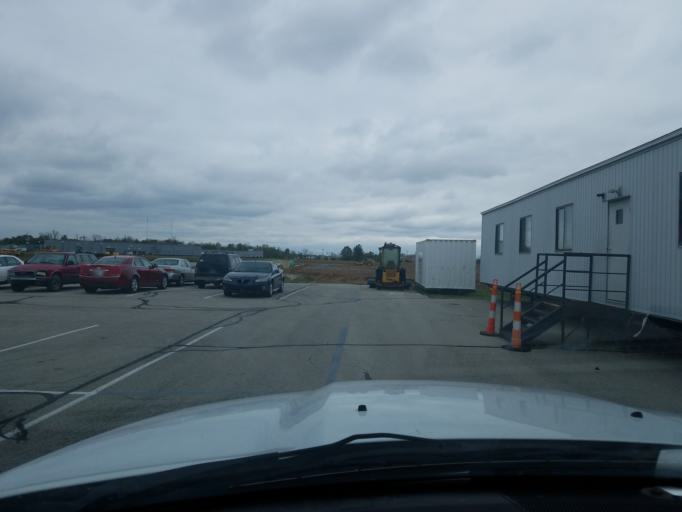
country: US
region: Indiana
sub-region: Clark County
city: Clarksville
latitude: 38.3285
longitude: -85.7480
